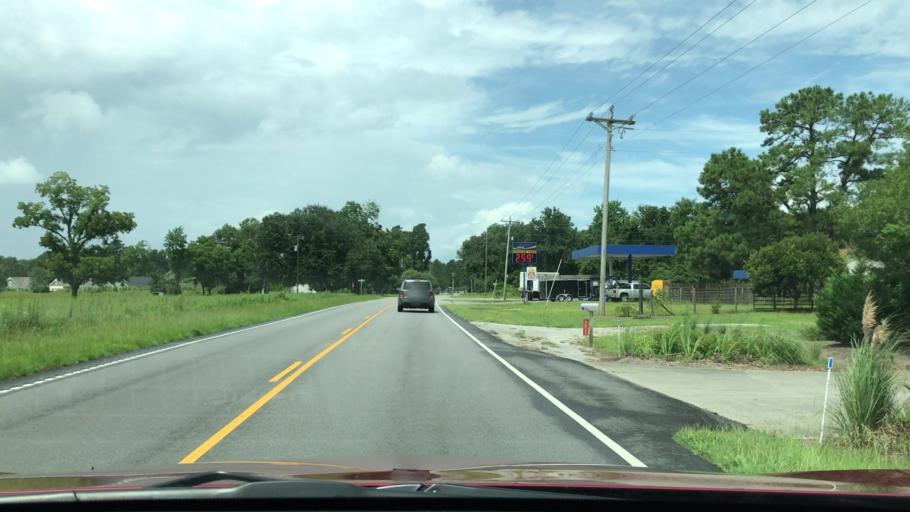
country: US
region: South Carolina
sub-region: Horry County
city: Red Hill
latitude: 33.9021
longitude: -78.8930
